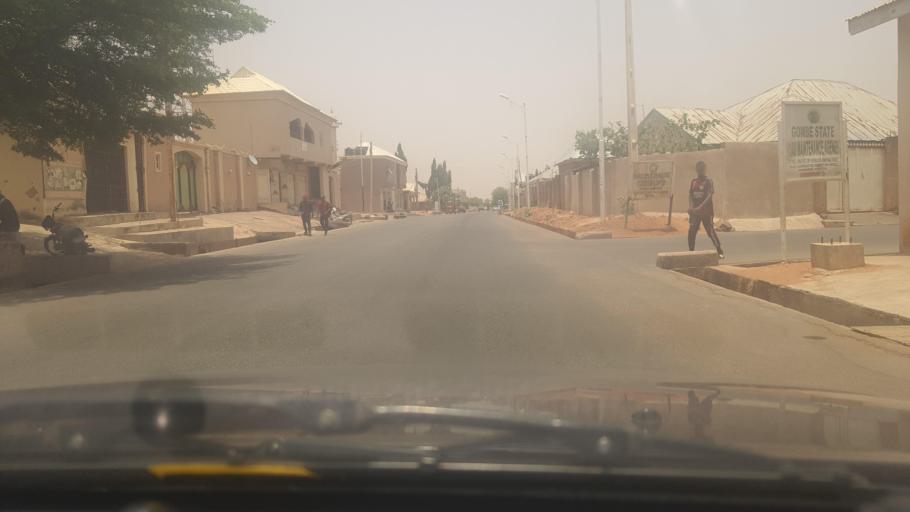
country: NG
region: Gombe
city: Gombe
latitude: 10.3047
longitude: 11.1480
